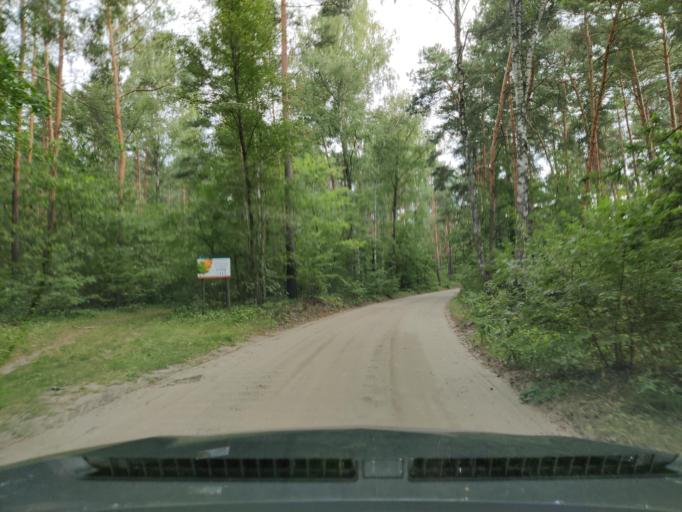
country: PL
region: Masovian Voivodeship
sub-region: Powiat pultuski
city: Pultusk
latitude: 52.7566
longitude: 21.1418
